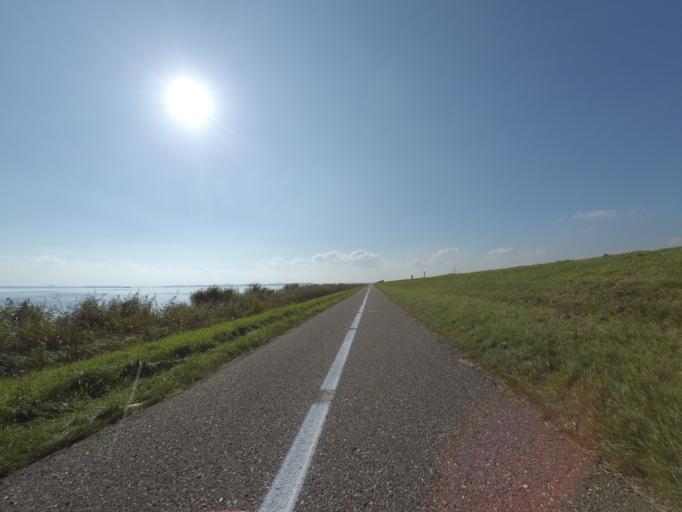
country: NL
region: Flevoland
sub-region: Gemeente Zeewolde
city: Zeewolde
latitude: 52.3629
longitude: 5.5567
